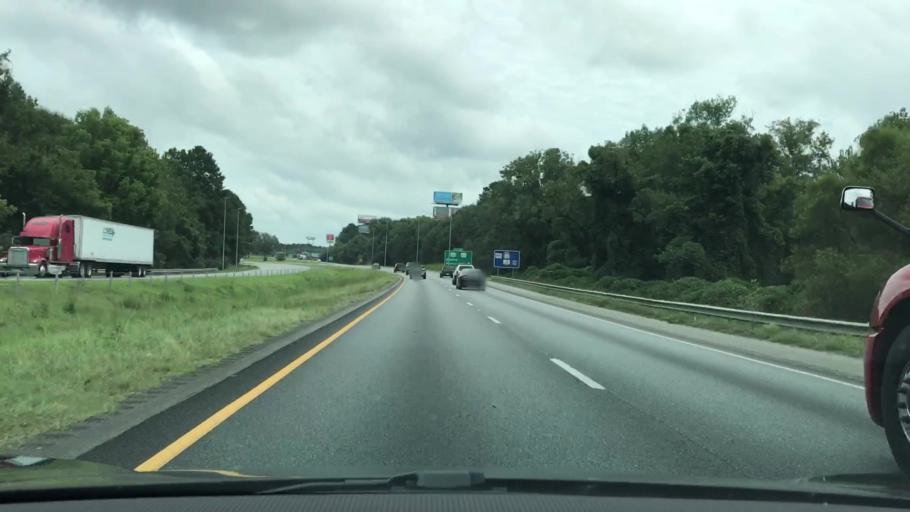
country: US
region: Alabama
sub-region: Lee County
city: Opelika
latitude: 32.6393
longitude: -85.3574
